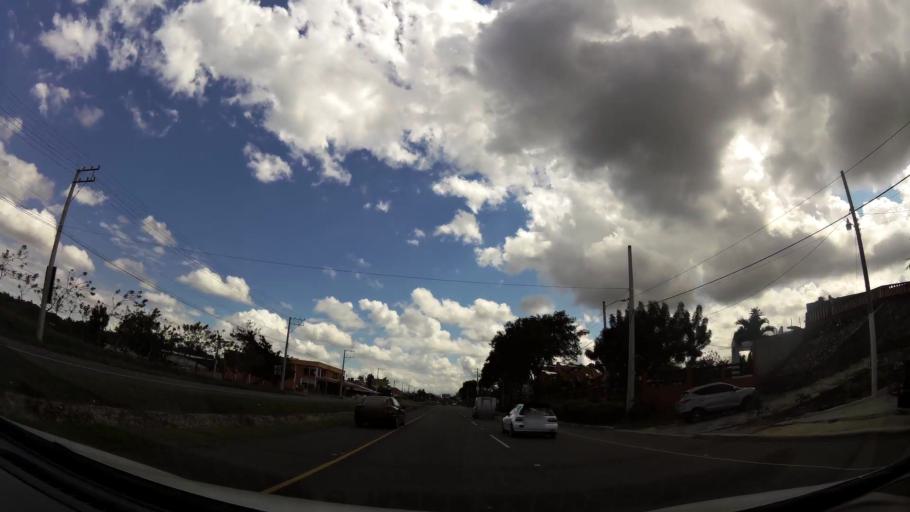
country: DO
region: La Vega
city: Rio Verde Arriba
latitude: 19.3579
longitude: -70.6016
